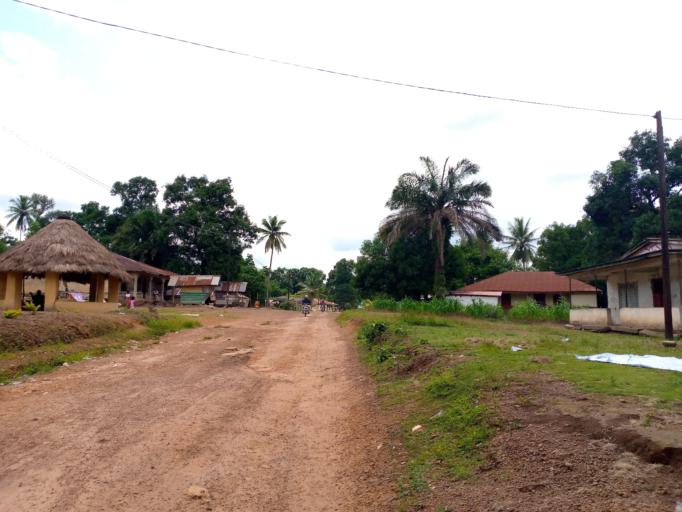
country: SL
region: Northern Province
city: Magburaka
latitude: 8.7118
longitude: -11.9345
